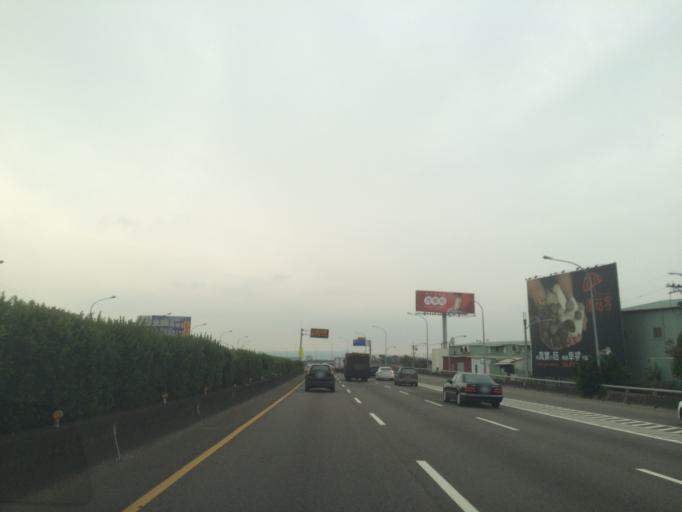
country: TW
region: Taiwan
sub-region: Taichung City
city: Taichung
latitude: 24.1328
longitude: 120.6204
